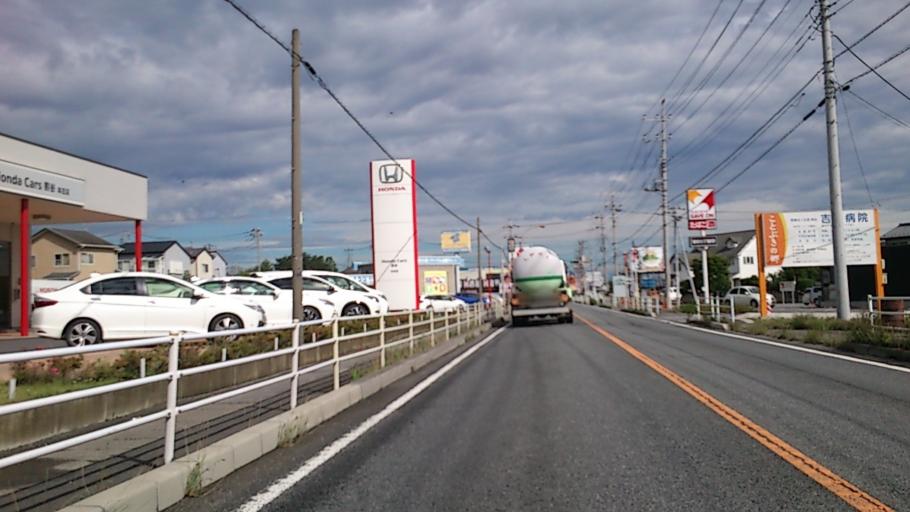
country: JP
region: Saitama
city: Honjo
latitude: 36.2385
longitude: 139.2050
